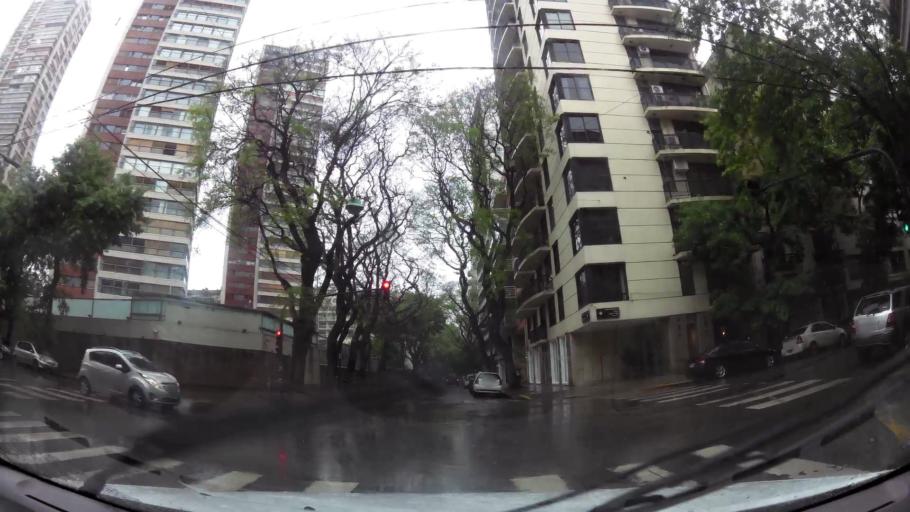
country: AR
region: Buenos Aires F.D.
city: Retiro
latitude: -34.5781
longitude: -58.4105
